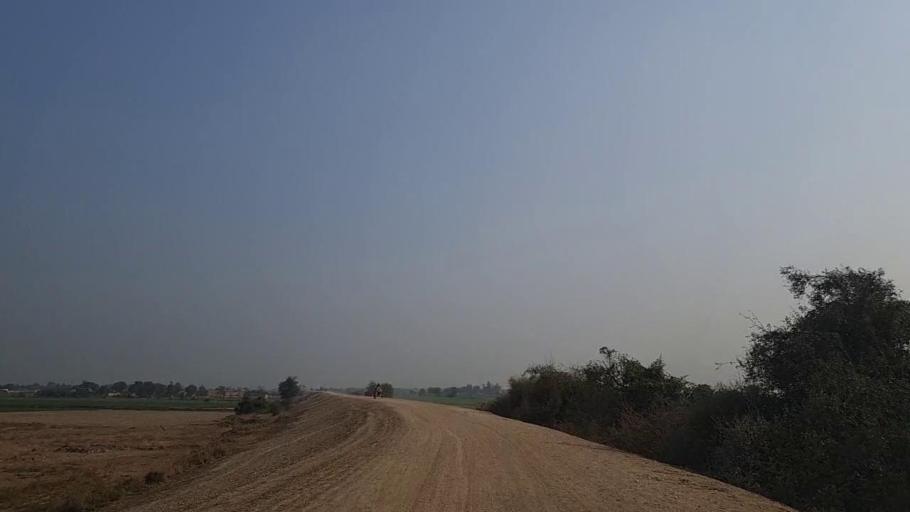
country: PK
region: Sindh
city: Sann
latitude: 26.0936
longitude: 68.1478
